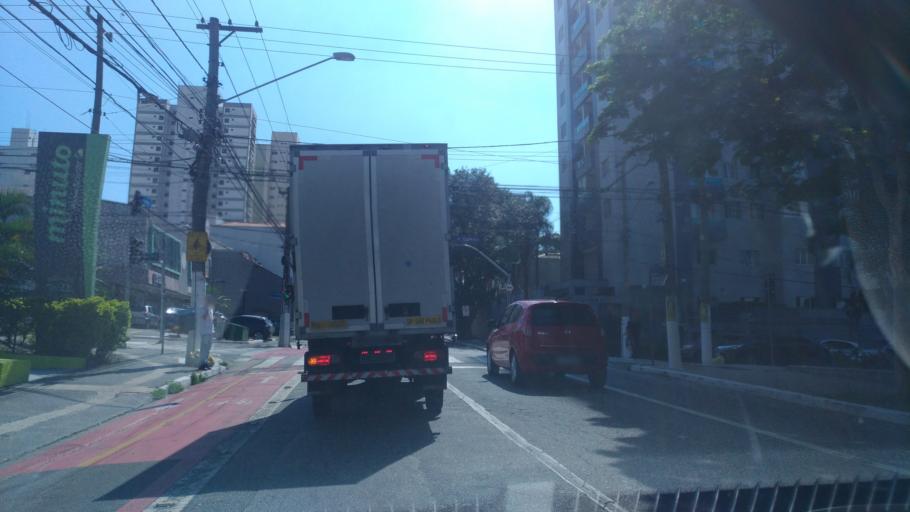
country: BR
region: Sao Paulo
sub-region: Sao Paulo
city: Sao Paulo
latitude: -23.5833
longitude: -46.6042
